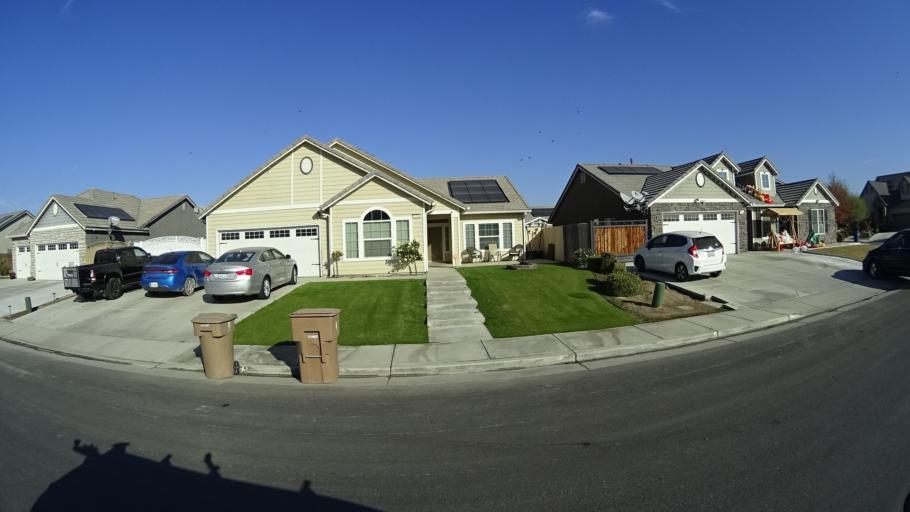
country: US
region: California
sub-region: Kern County
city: Greenfield
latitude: 35.2720
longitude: -119.0667
